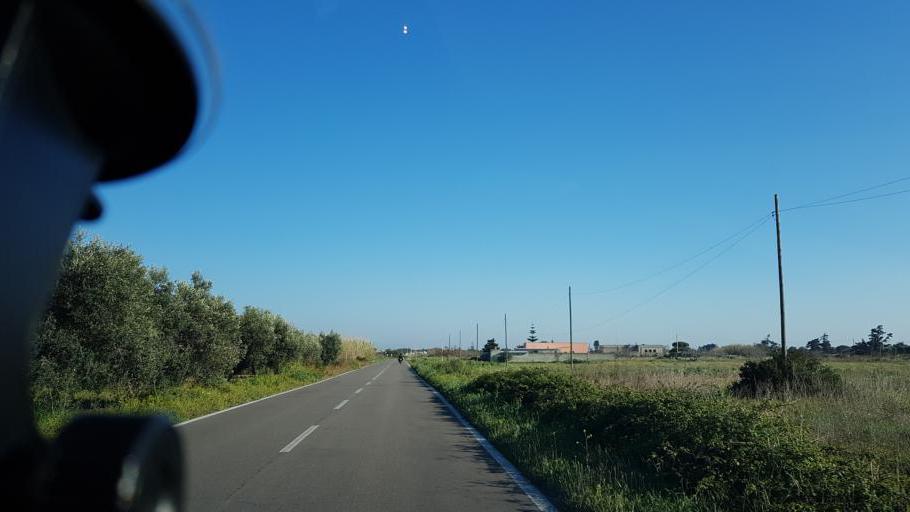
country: IT
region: Apulia
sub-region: Provincia di Lecce
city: Giorgilorio
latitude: 40.4389
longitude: 18.2366
